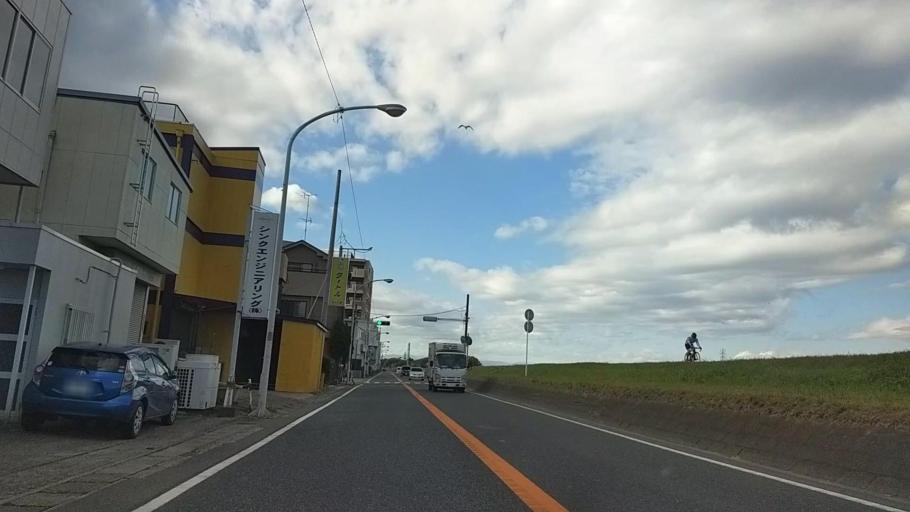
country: JP
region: Tokyo
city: Chofugaoka
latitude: 35.6125
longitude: 139.6110
